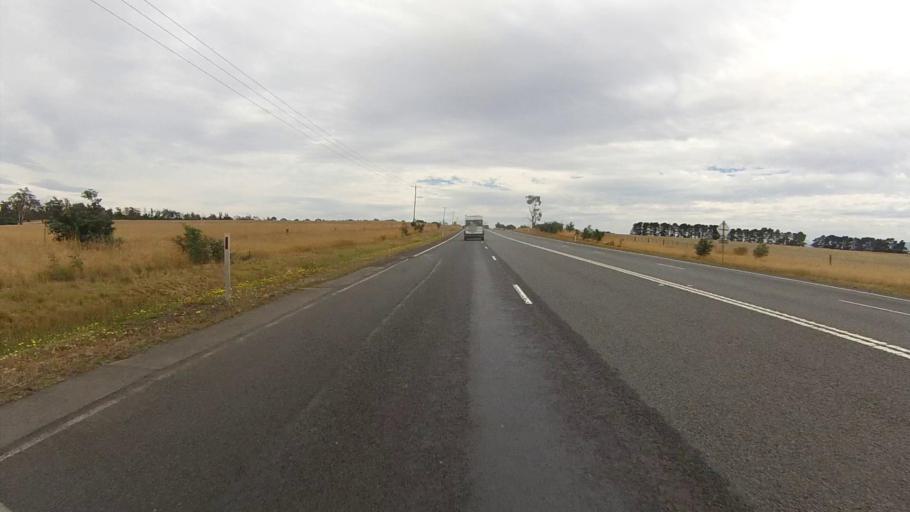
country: AU
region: Tasmania
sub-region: Northern Midlands
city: Evandale
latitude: -41.7143
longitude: 147.3053
